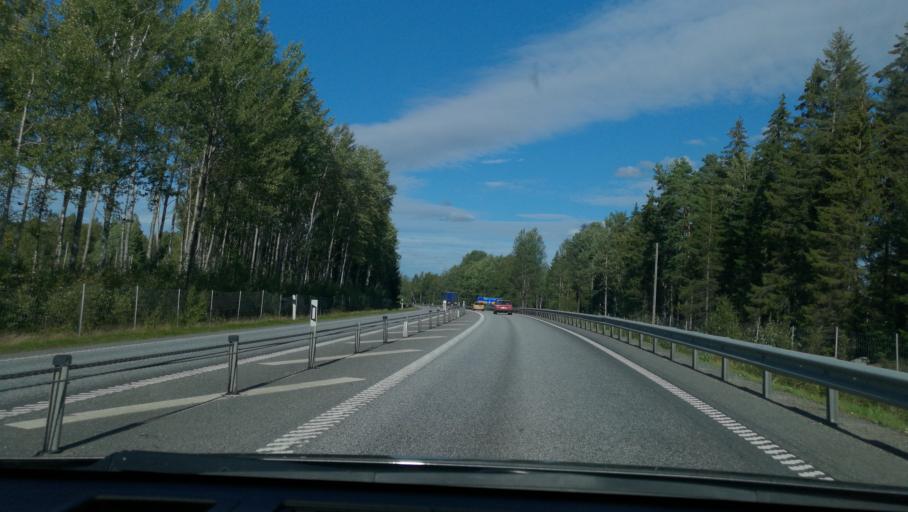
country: SE
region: OErebro
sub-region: Laxa Kommun
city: Laxa
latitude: 58.9619
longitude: 14.5325
